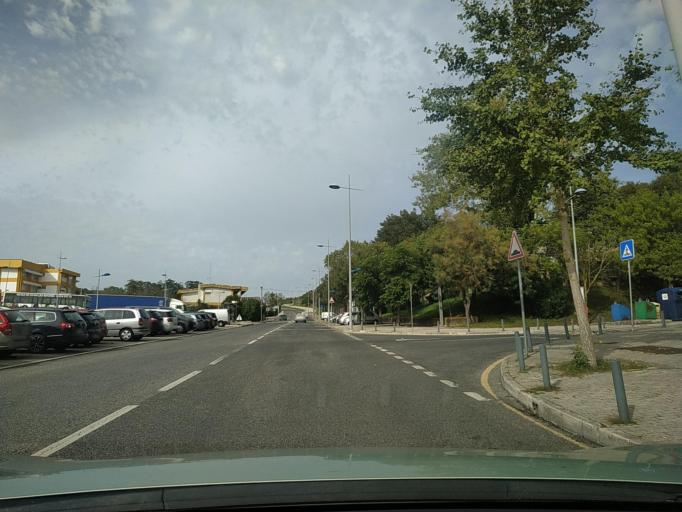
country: PT
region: Lisbon
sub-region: Amadora
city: Amadora
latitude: 38.7681
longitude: -9.2393
